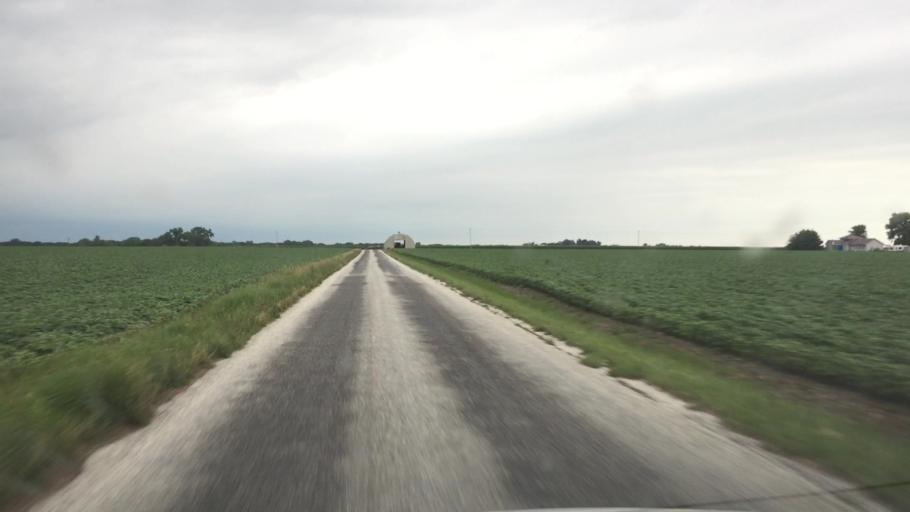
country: US
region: Illinois
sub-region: Adams County
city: Camp Point
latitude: 40.2262
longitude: -90.9690
